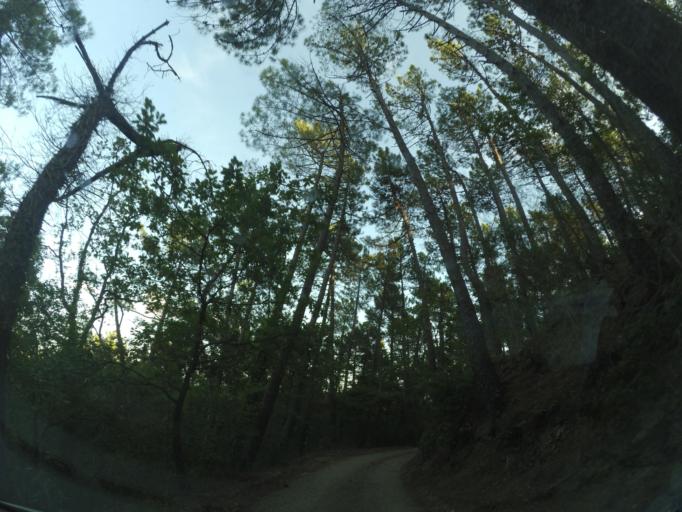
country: IT
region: Tuscany
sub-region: Province of Arezzo
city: Castiglion Fibocchi
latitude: 43.5500
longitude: 11.7882
